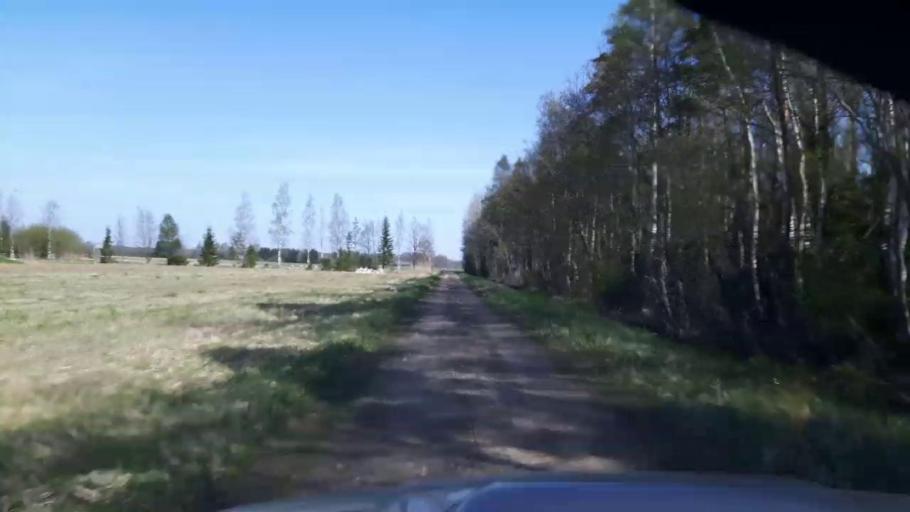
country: EE
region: Paernumaa
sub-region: Tootsi vald
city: Tootsi
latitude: 58.4794
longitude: 24.9256
